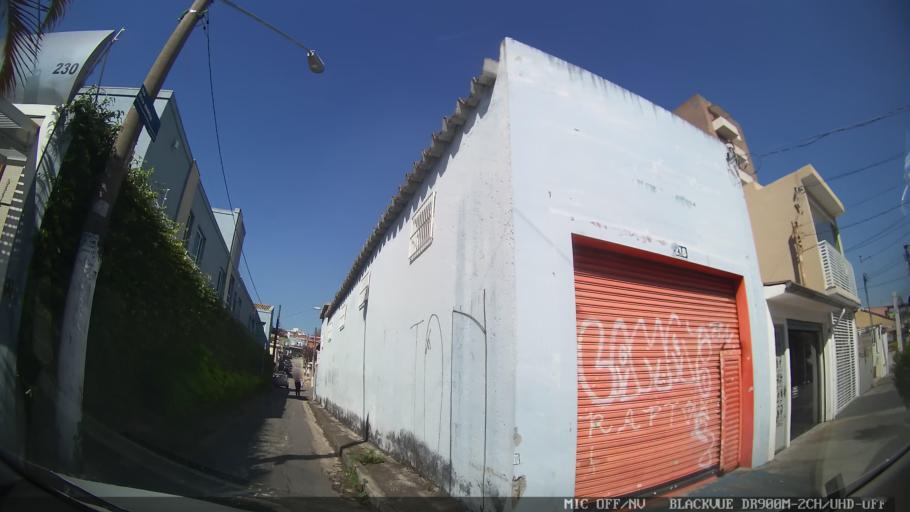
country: BR
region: Sao Paulo
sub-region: Sao Paulo
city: Sao Paulo
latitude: -23.5107
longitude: -46.6618
